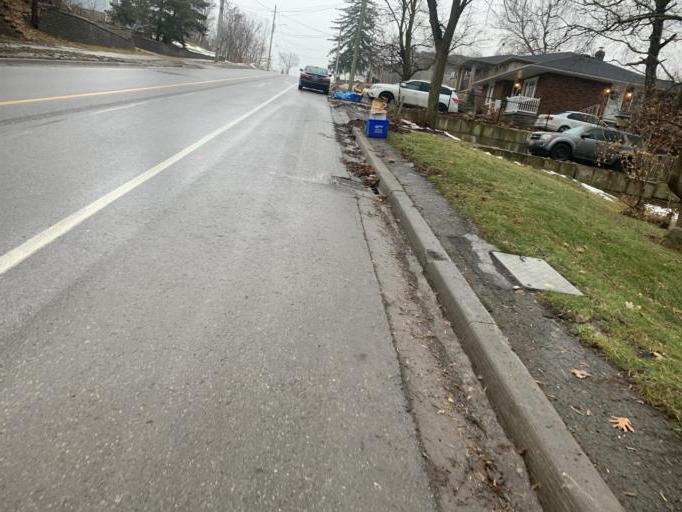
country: CA
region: Ontario
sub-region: Halton
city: Milton
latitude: 43.6582
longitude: -79.9195
